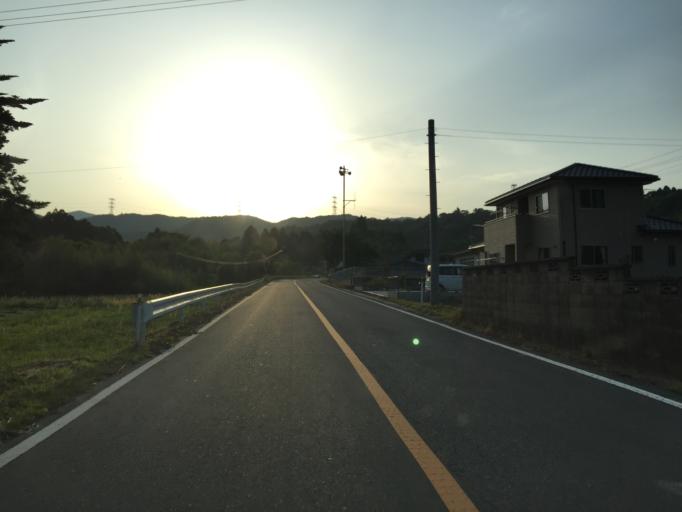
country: JP
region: Fukushima
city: Iwaki
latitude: 37.2198
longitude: 140.9723
